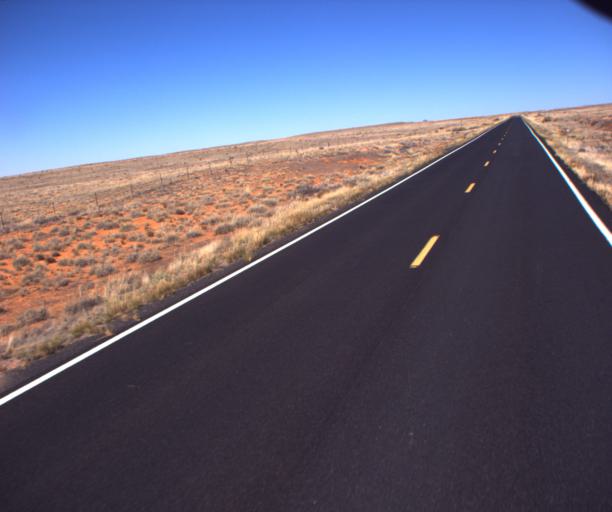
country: US
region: Arizona
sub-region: Navajo County
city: Dilkon
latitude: 35.2705
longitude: -110.4293
